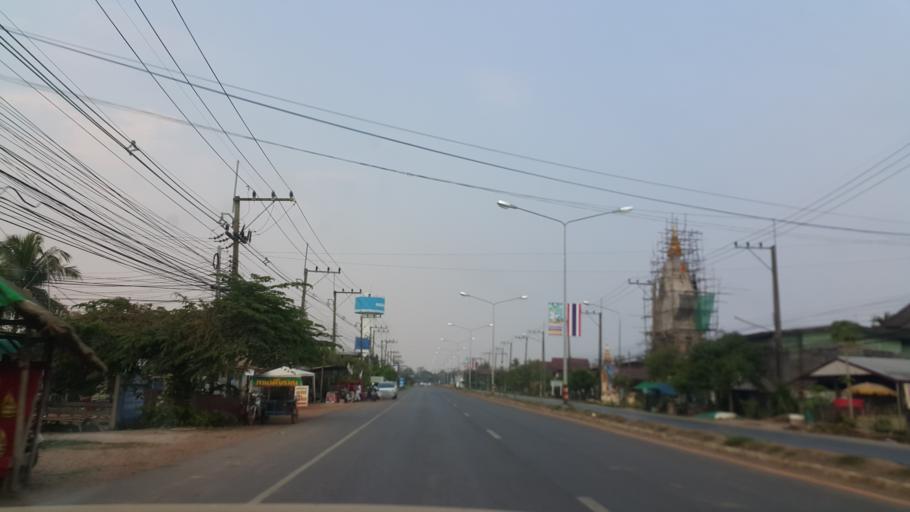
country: TH
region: Nakhon Phanom
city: That Phanom
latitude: 16.9794
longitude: 104.7279
